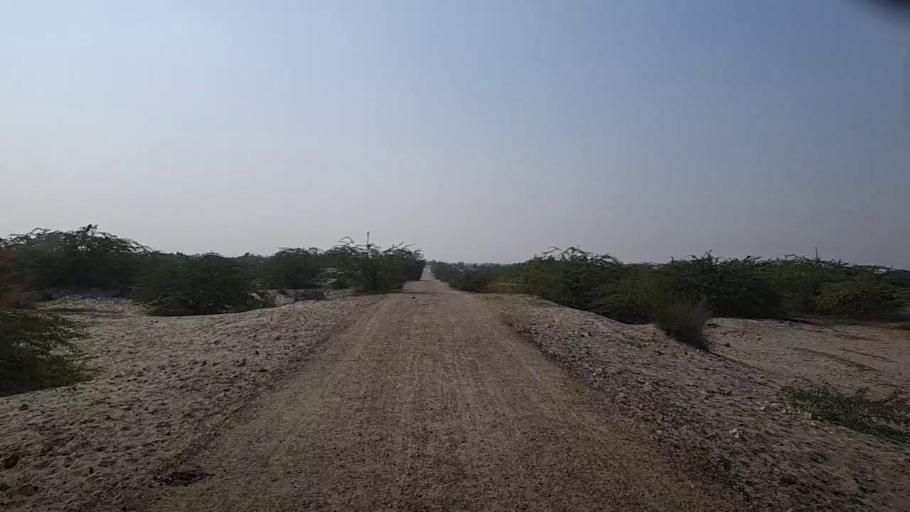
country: PK
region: Sindh
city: Bozdar
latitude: 27.2338
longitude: 68.5955
